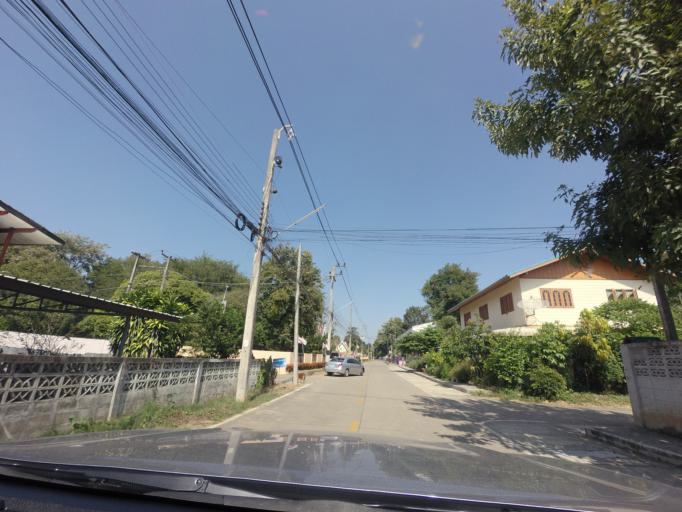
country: TH
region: Sukhothai
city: Sawankhalok
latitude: 17.3186
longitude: 99.8263
